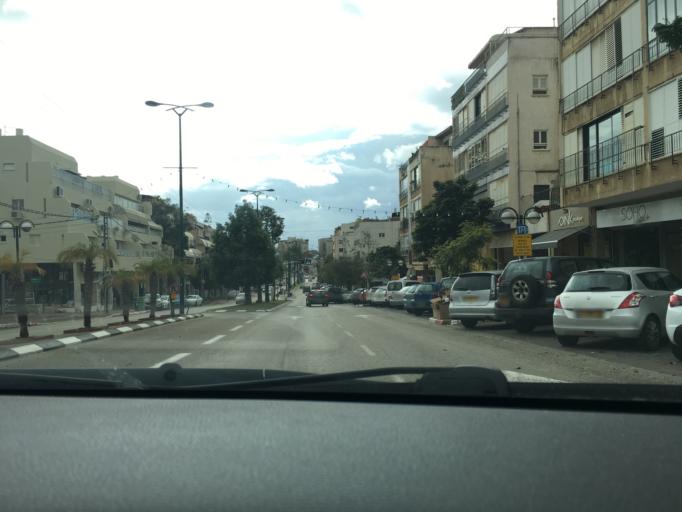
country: IL
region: Tel Aviv
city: Ramat HaSharon
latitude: 32.1405
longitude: 34.8425
